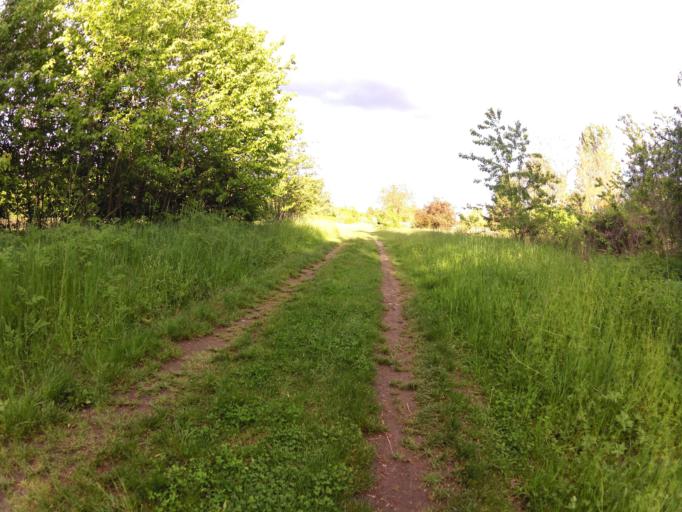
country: DE
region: Bavaria
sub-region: Regierungsbezirk Unterfranken
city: Volkach
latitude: 49.8705
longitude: 10.2118
